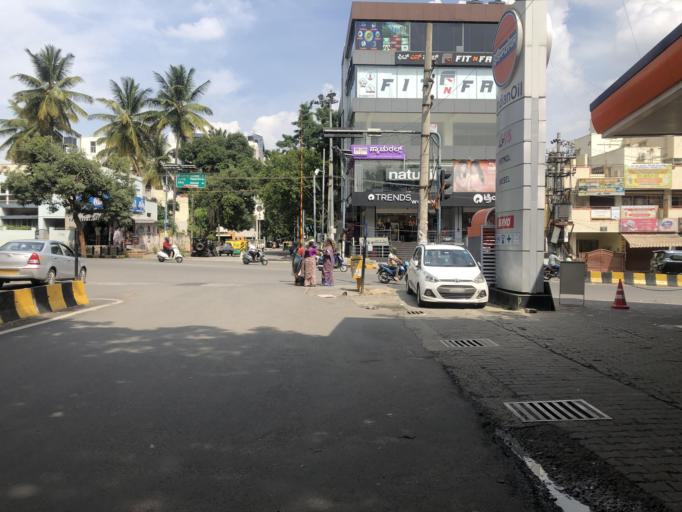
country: IN
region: Karnataka
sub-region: Bangalore Urban
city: Bangalore
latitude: 12.9381
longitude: 77.5495
